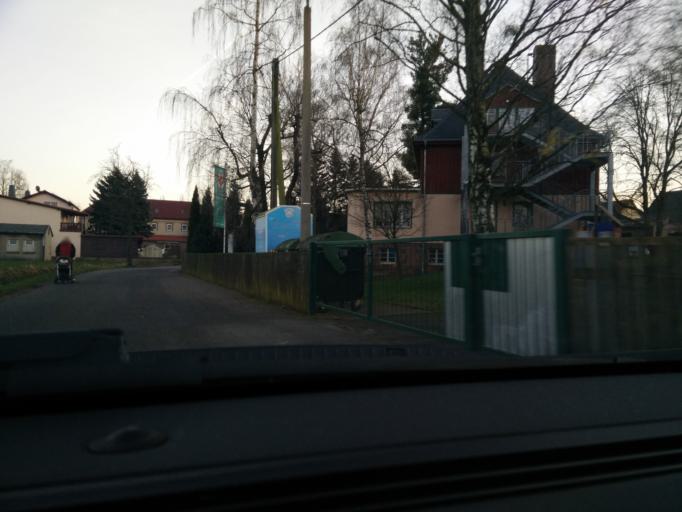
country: DE
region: Saxony
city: Geithain
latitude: 51.0517
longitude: 12.6952
